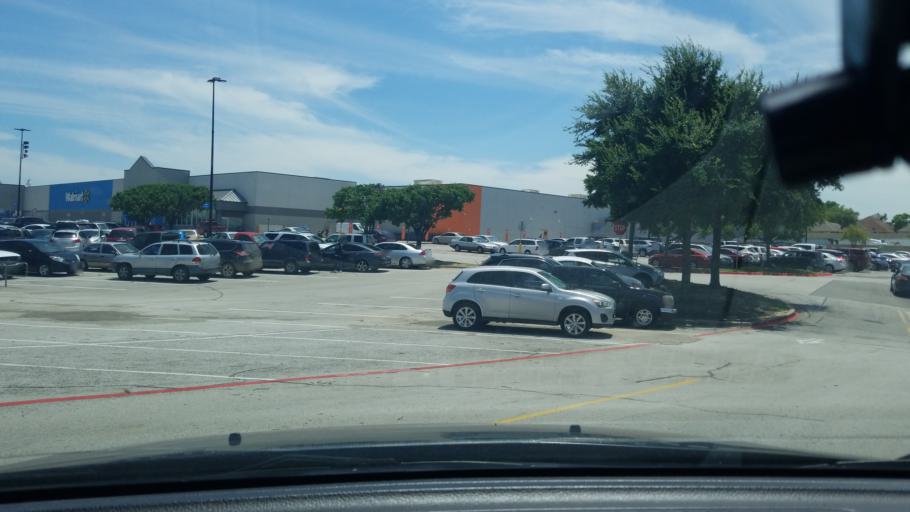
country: US
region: Texas
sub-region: Dallas County
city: Mesquite
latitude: 32.7905
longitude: -96.5996
